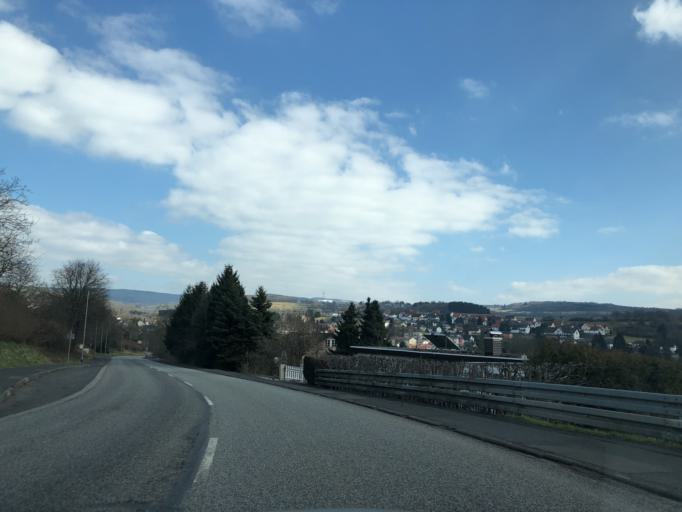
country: DE
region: Hesse
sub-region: Regierungsbezirk Giessen
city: Schotten
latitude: 50.5067
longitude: 9.1242
